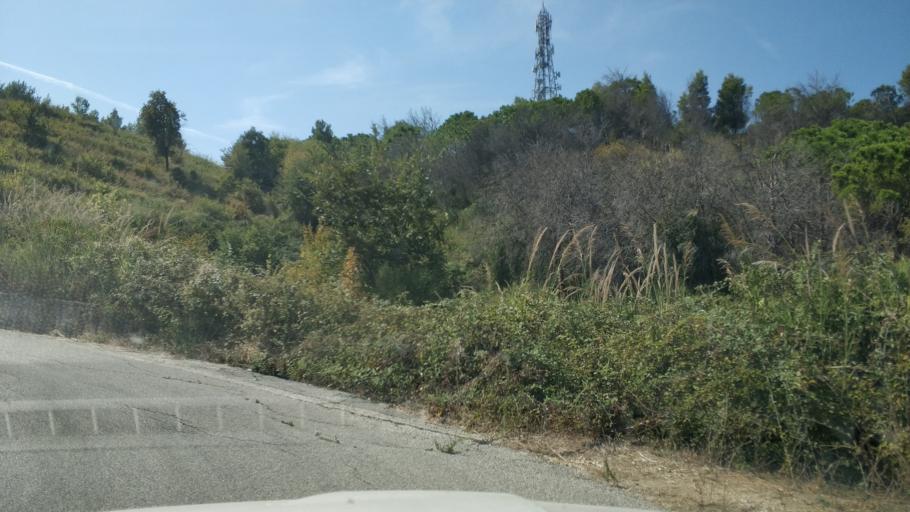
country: AL
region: Fier
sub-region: Rrethi i Lushnjes
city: Kolonje
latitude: 40.8239
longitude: 19.5962
